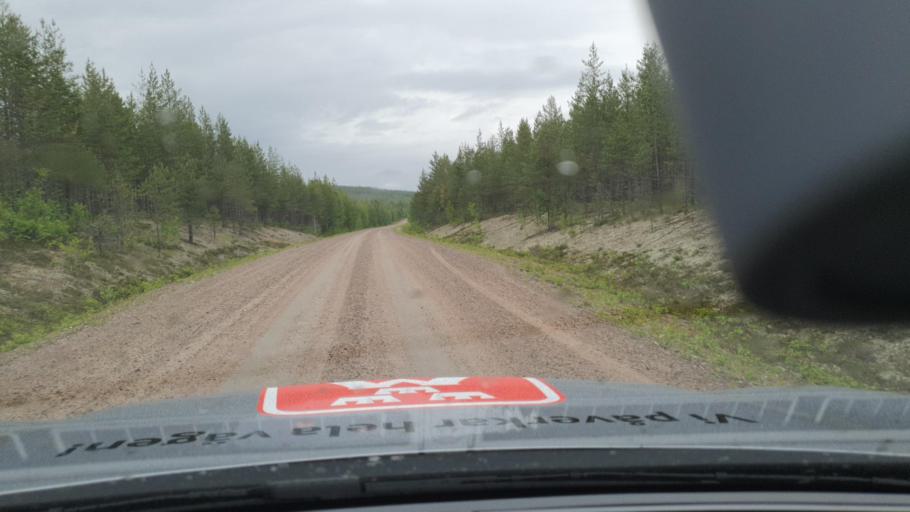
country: SE
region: Norrbotten
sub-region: Overkalix Kommun
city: OEverkalix
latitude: 66.5780
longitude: 22.7451
